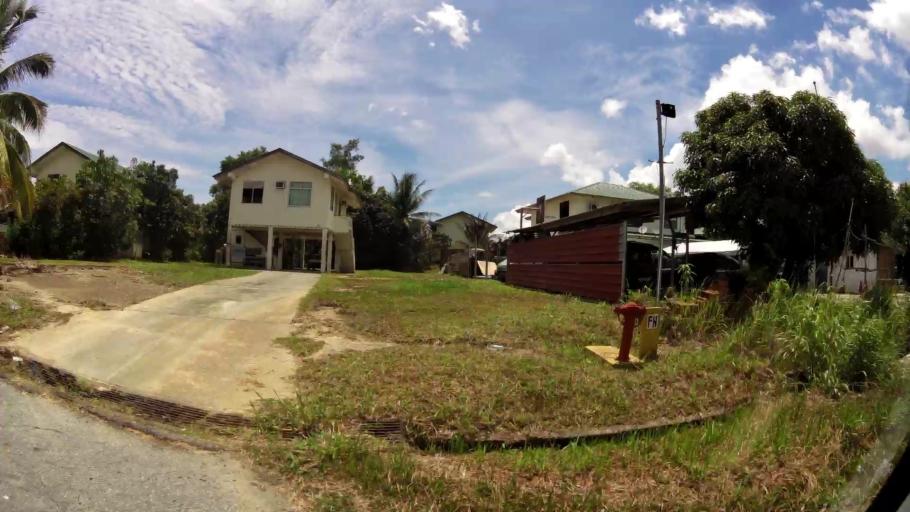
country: BN
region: Brunei and Muara
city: Bandar Seri Begawan
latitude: 4.9590
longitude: 114.9048
